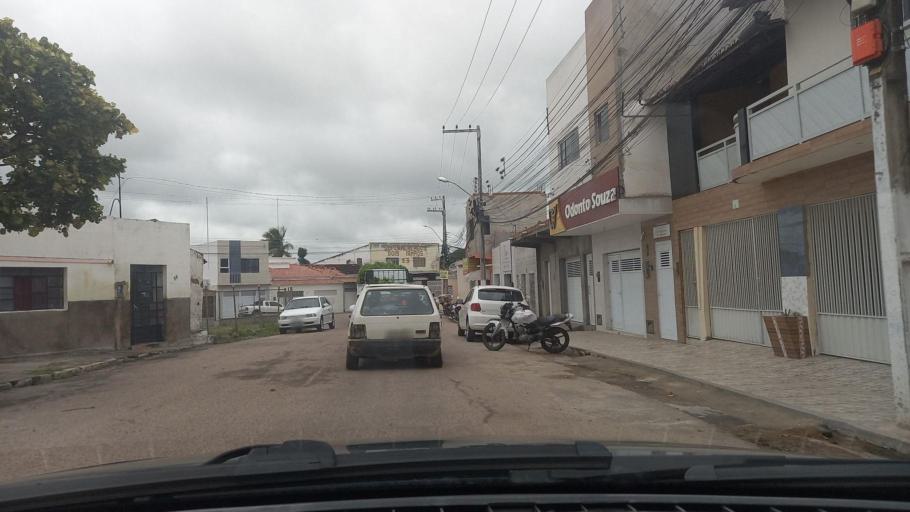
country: BR
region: Alagoas
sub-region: Delmiro Gouveia
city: Delmiro Gouveia
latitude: -9.3866
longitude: -37.9942
